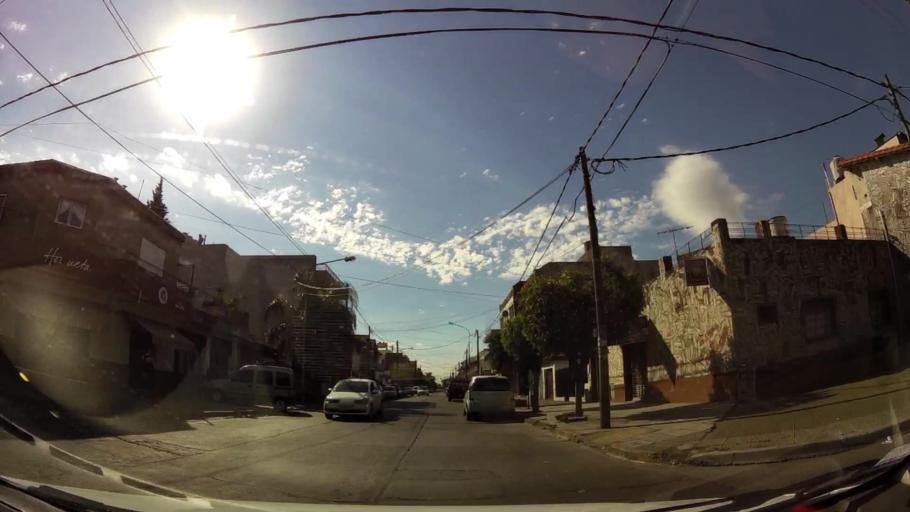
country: AR
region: Buenos Aires
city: San Justo
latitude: -34.6662
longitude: -58.5771
